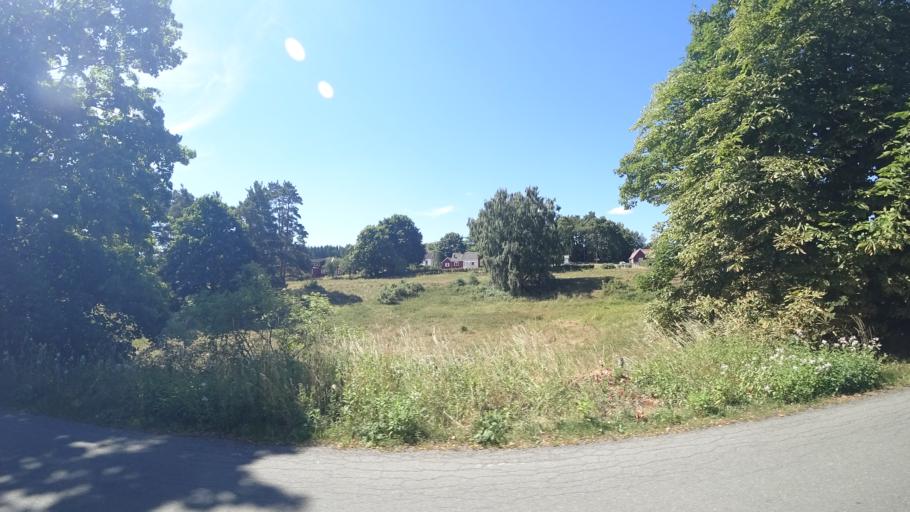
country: SE
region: Skane
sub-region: Kristianstads Kommun
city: Onnestad
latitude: 56.0476
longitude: 14.0250
